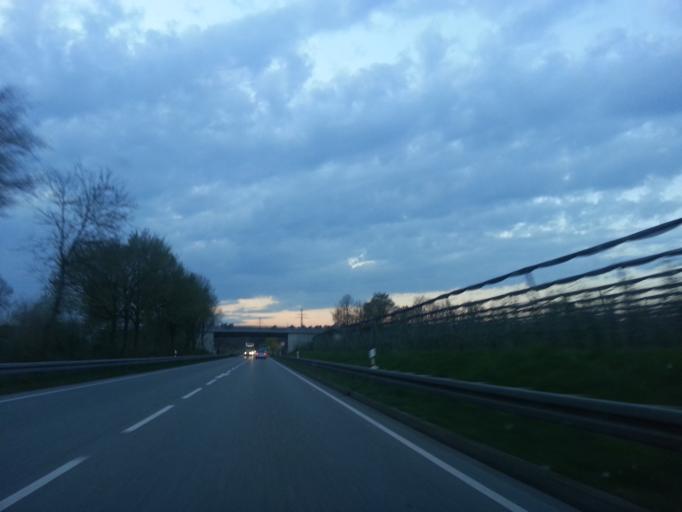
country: DE
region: Baden-Wuerttemberg
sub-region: Tuebingen Region
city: Eriskirch
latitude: 47.6135
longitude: 9.5700
